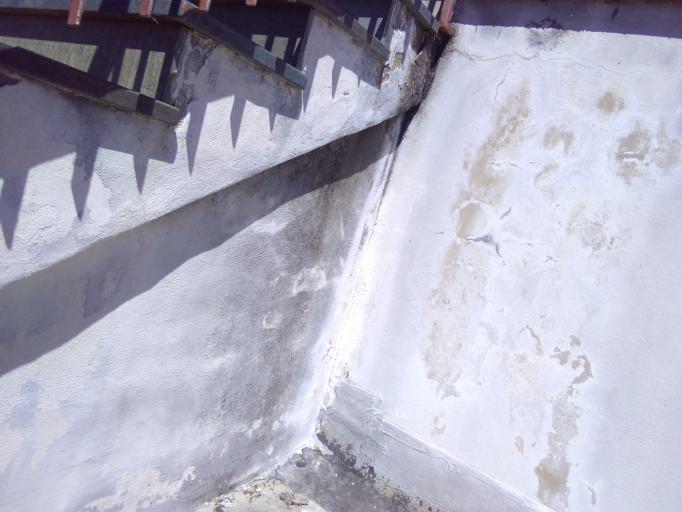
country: IT
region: Emilia-Romagna
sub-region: Provincia di Parma
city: Calestano
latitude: 44.5868
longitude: 10.1589
